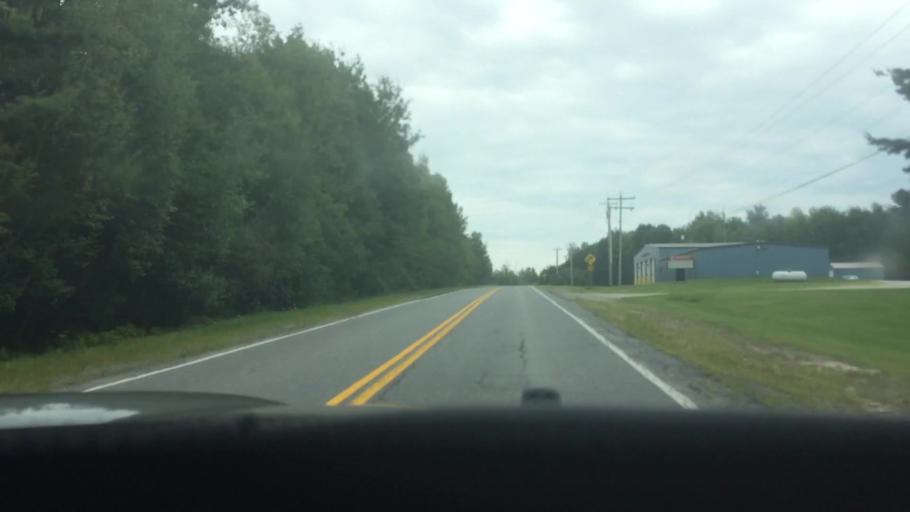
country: US
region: New York
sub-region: St. Lawrence County
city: Hannawa Falls
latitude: 44.5380
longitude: -75.0114
